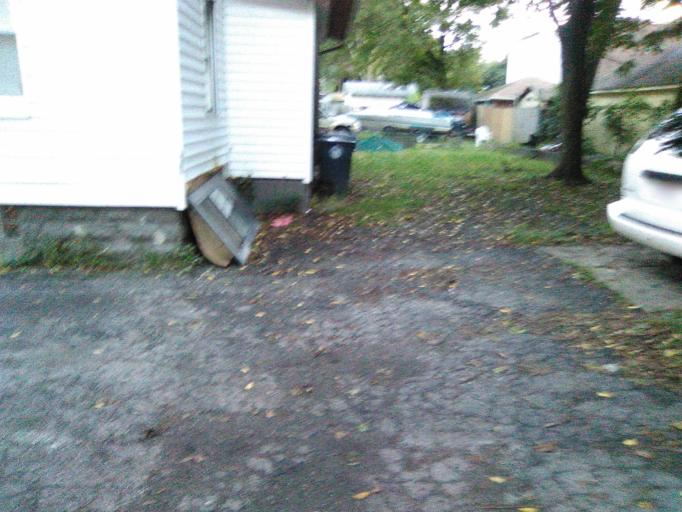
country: US
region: Ohio
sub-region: Summit County
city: Akron
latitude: 41.0936
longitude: -81.5495
